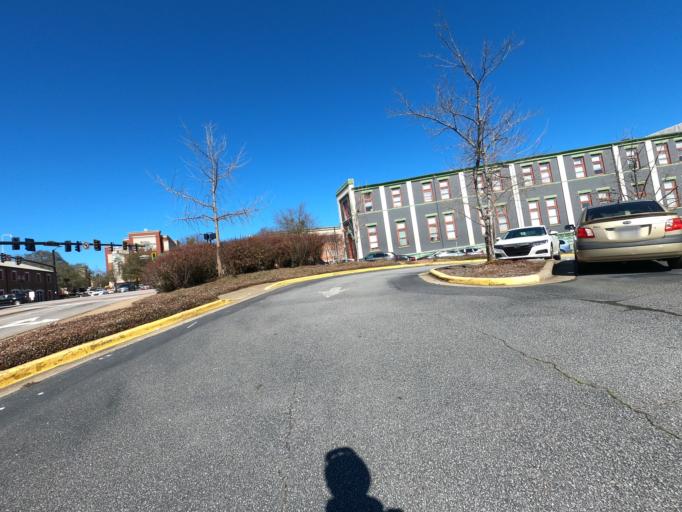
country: US
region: Georgia
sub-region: Clarke County
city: Athens
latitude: 33.9579
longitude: -83.3725
